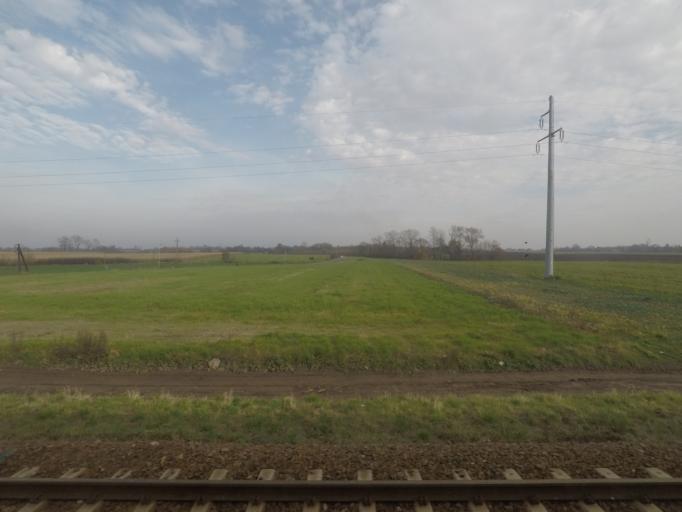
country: PL
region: Subcarpathian Voivodeship
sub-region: Powiat jaroslawski
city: Sosnica
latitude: 49.8975
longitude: 22.8533
